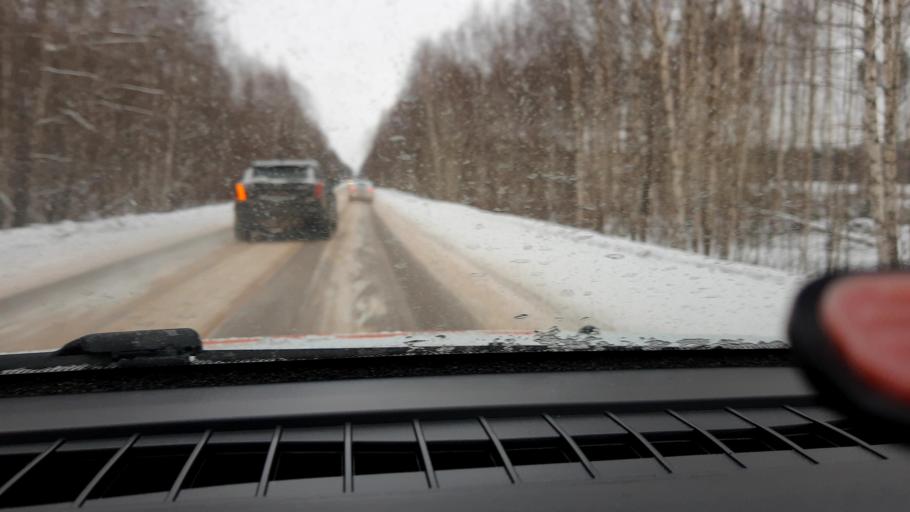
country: RU
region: Nizjnij Novgorod
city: Pamyat' Parizhskoy Kommuny
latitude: 56.2757
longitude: 44.3977
